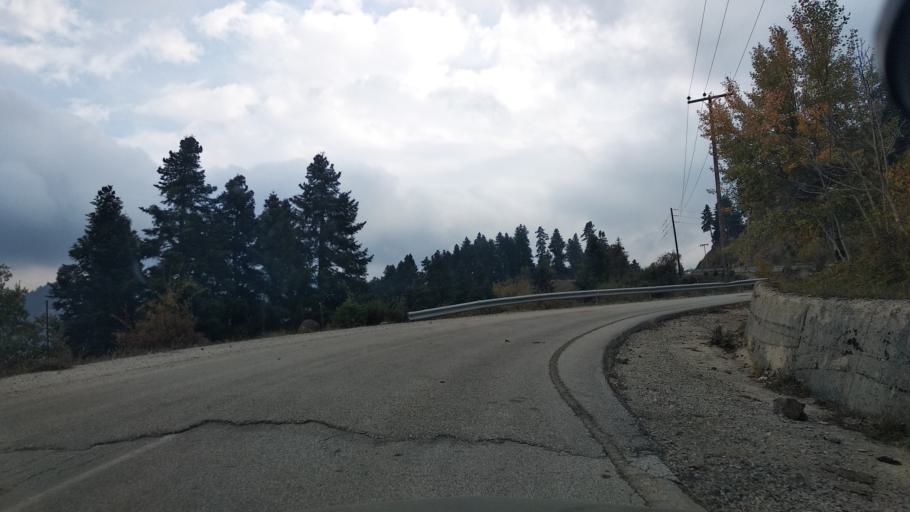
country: GR
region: Thessaly
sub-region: Trikala
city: Kalampaka
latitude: 39.5883
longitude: 21.4910
